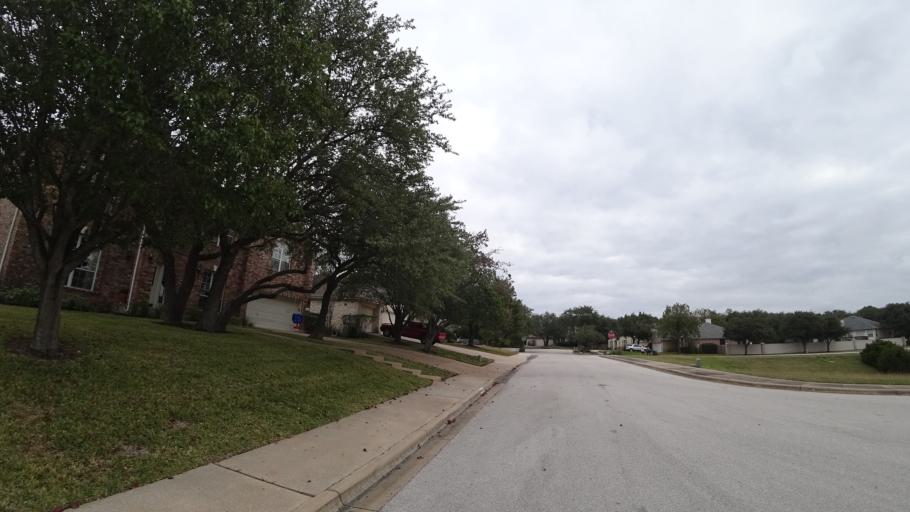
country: US
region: Texas
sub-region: Travis County
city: Bee Cave
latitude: 30.3103
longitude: -97.9263
